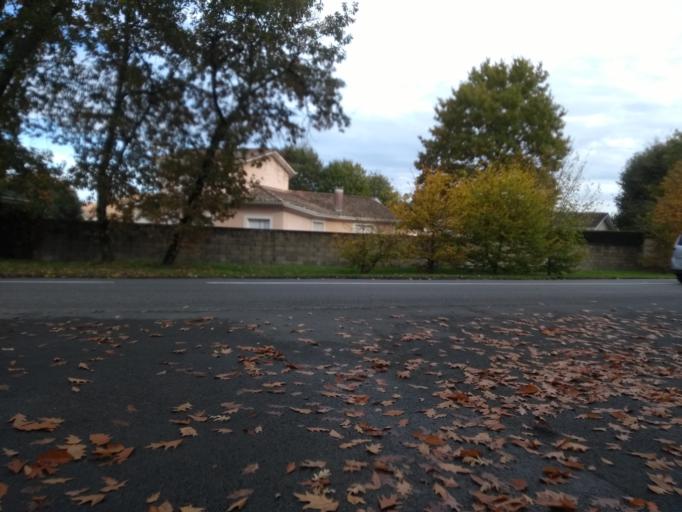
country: FR
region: Aquitaine
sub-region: Departement de la Gironde
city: Cestas
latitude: 44.7379
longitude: -0.6757
